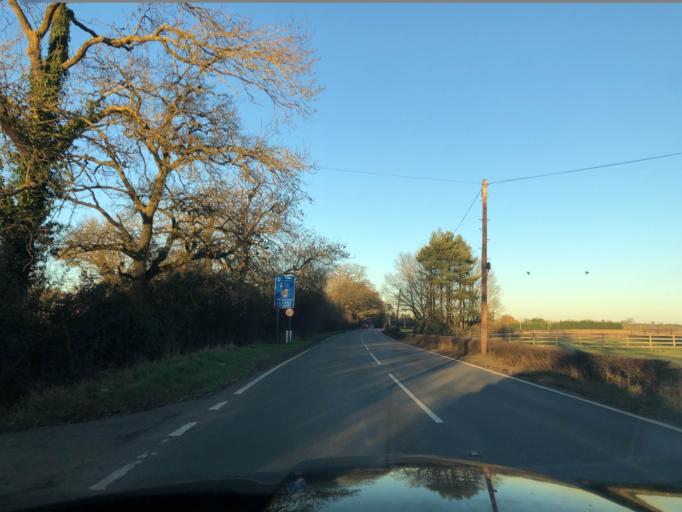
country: GB
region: England
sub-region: Warwickshire
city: Harbury
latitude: 52.2026
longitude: -1.4476
